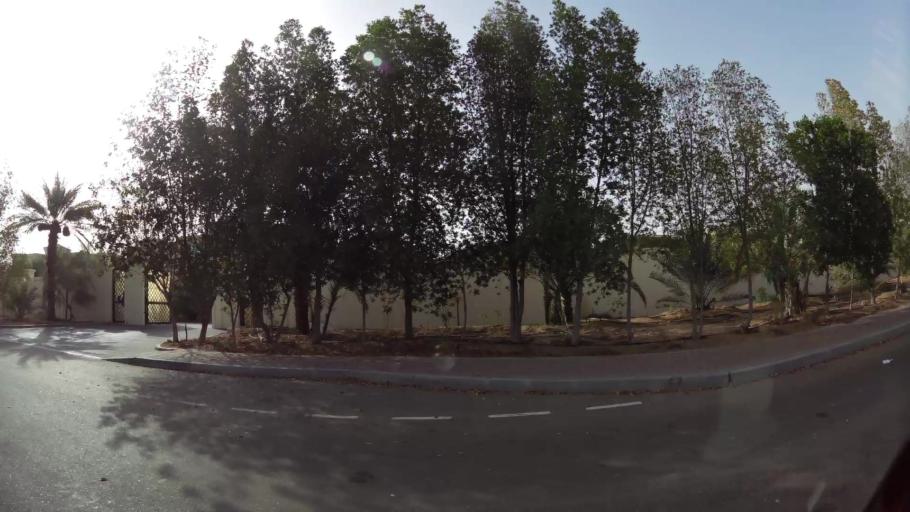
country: AE
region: Abu Dhabi
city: Al Ain
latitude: 24.2081
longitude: 55.6191
